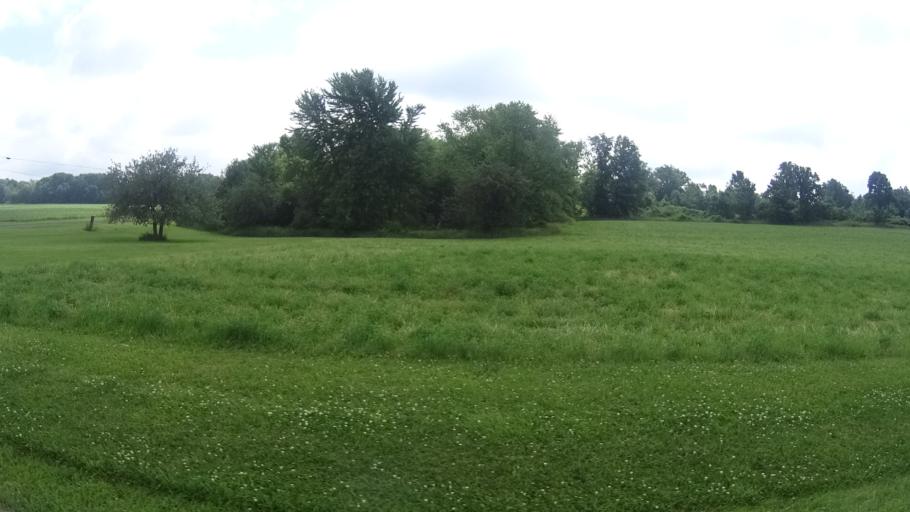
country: US
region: Ohio
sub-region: Huron County
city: Wakeman
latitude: 41.3027
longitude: -82.3875
